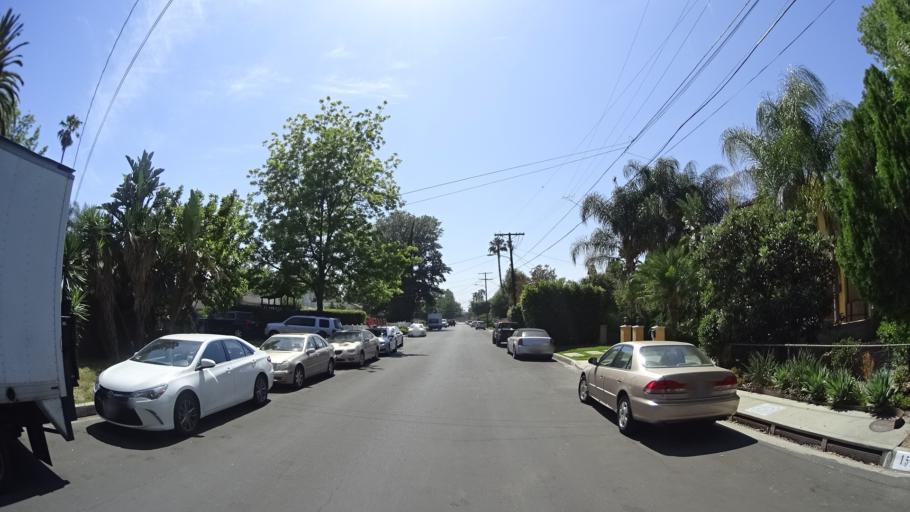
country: US
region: California
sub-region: Los Angeles County
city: Sherman Oaks
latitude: 34.1639
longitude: -118.4622
